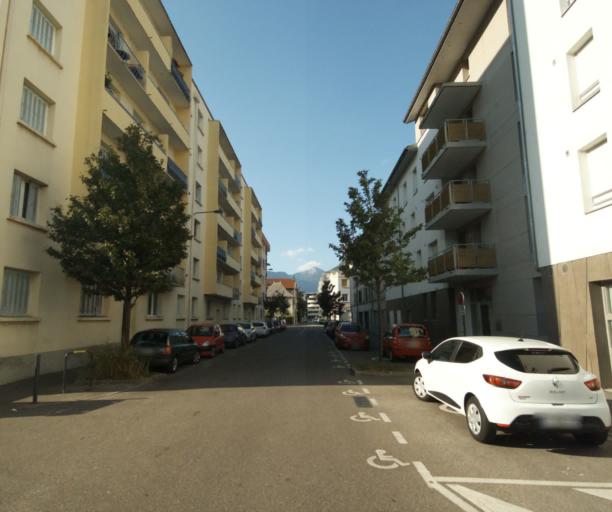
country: FR
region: Rhone-Alpes
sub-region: Departement de l'Isere
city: Seyssinet-Pariset
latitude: 45.1904
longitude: 5.6972
